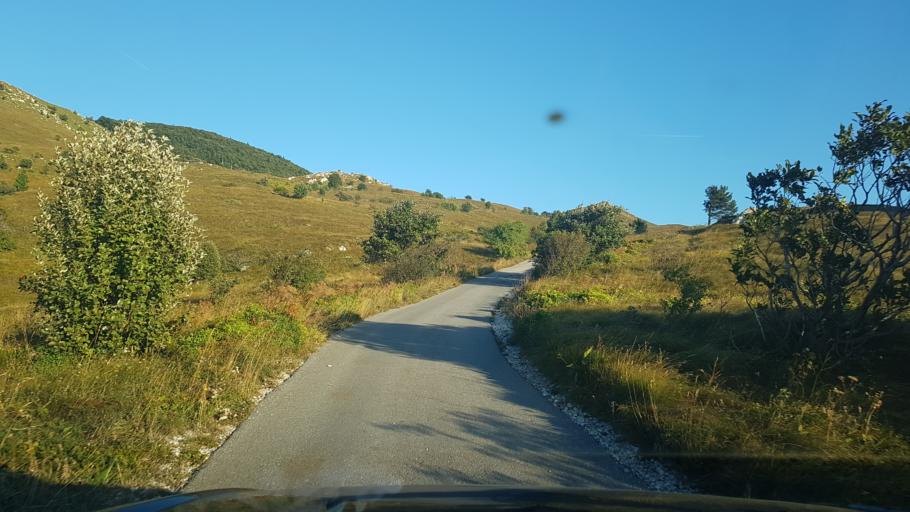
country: SI
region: Vipava
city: Vipava
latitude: 45.7856
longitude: 14.0299
